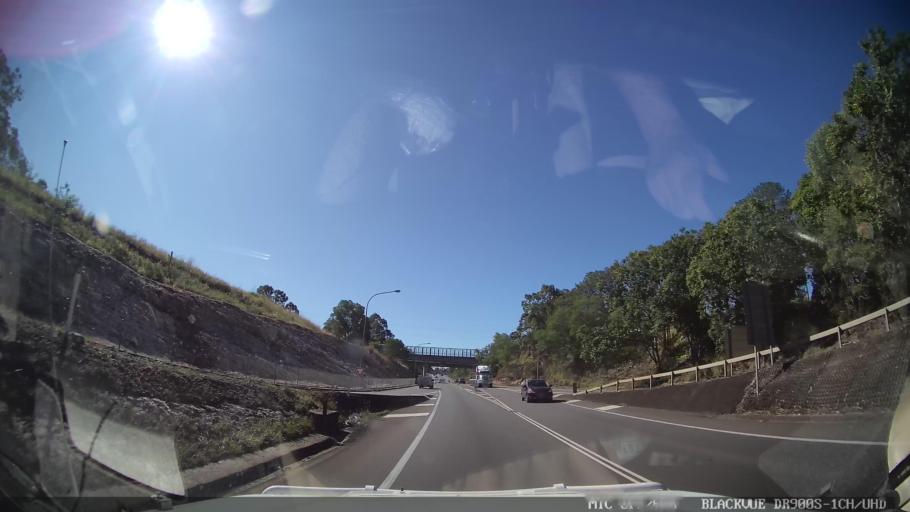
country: AU
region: Queensland
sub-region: Fraser Coast
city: Maryborough
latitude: -25.5186
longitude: 152.6692
